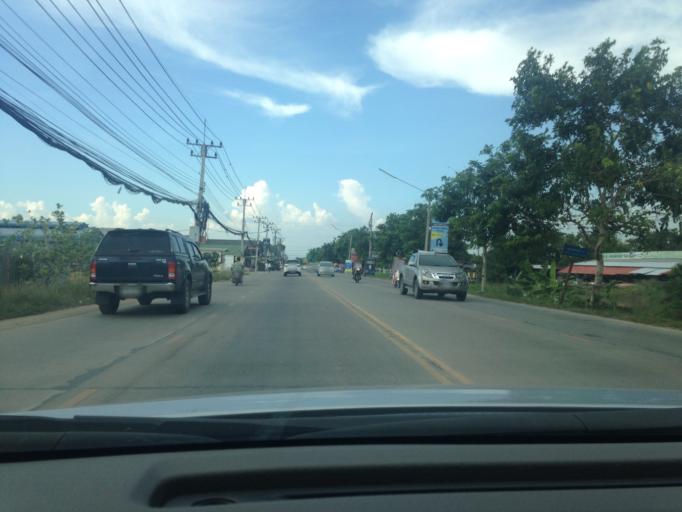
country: TH
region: Pathum Thani
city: Khlong Luang
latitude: 14.0461
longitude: 100.6636
